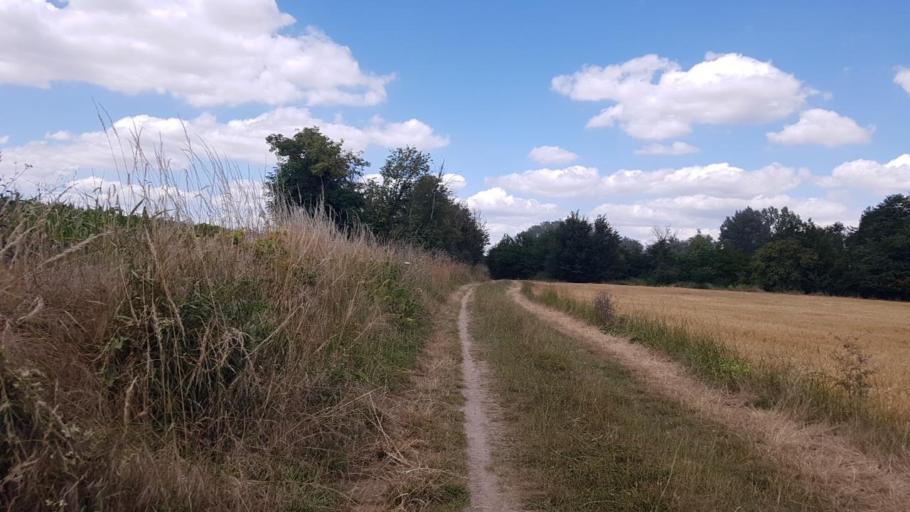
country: FR
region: Ile-de-France
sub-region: Departement de Seine-et-Marne
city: Claye-Souilly
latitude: 48.9749
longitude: 2.6696
